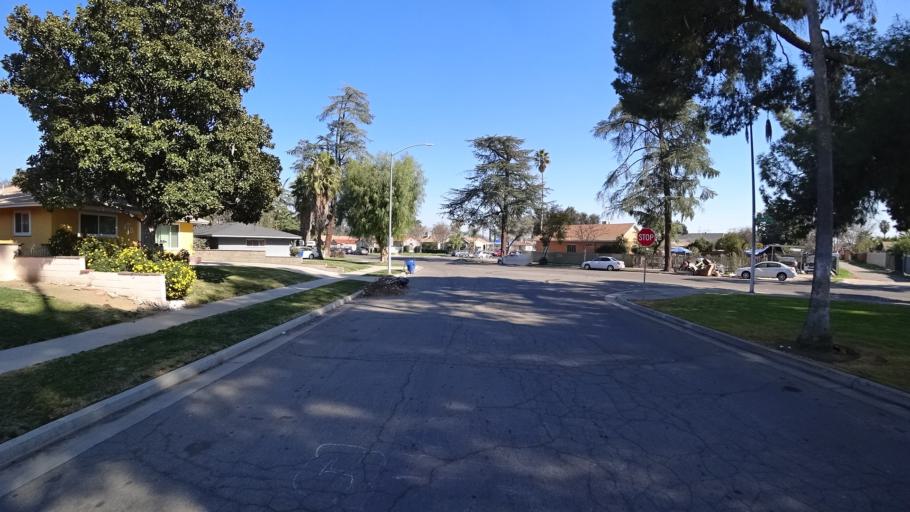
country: US
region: California
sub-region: Fresno County
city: Fresno
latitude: 36.7275
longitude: -119.8071
